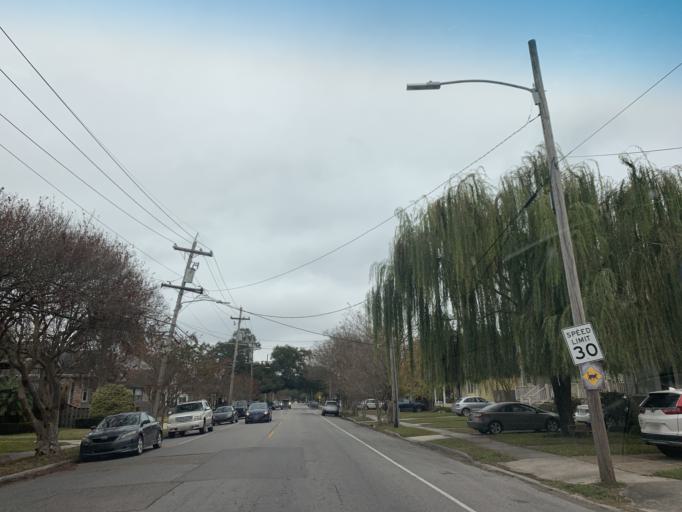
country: US
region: Louisiana
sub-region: Jefferson Parish
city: Metairie
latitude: 29.9898
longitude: -90.1092
